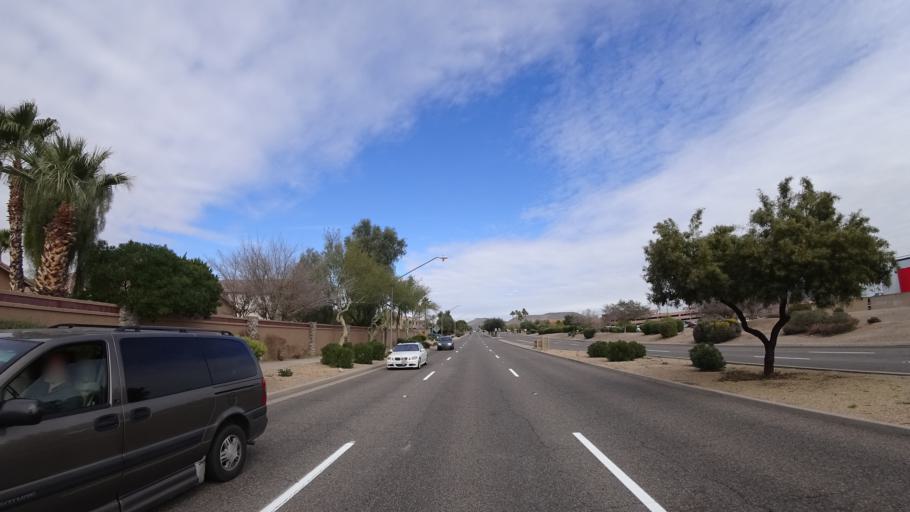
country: US
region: Arizona
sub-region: Maricopa County
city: Peoria
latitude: 33.6571
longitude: -112.1865
